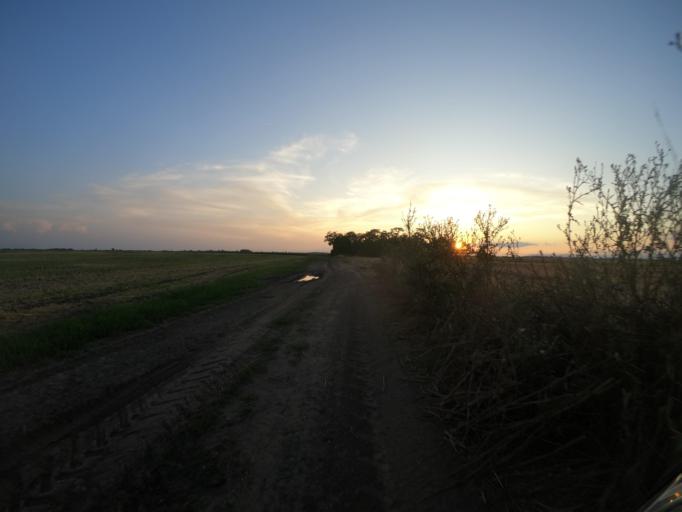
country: HU
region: Borsod-Abauj-Zemplen
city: Szentistvan
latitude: 47.7456
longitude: 20.7243
